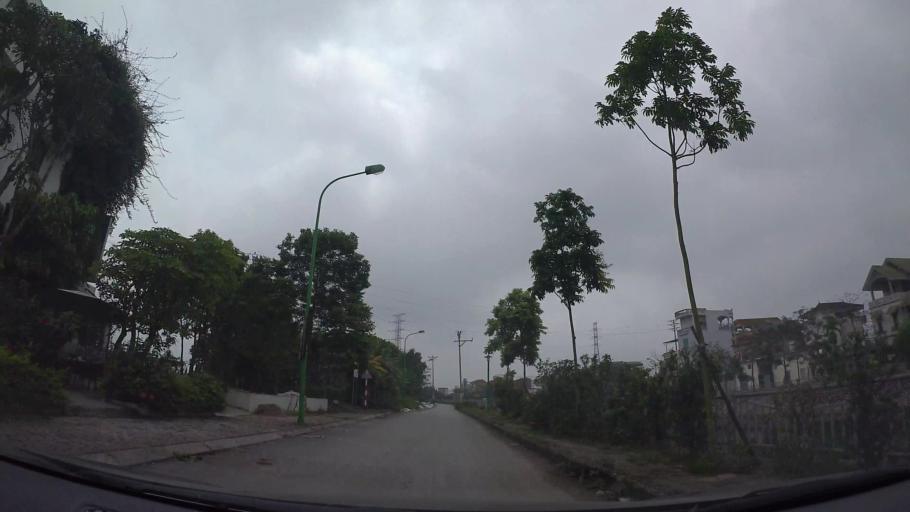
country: VN
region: Ha Noi
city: Van Dien
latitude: 20.9735
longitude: 105.8522
